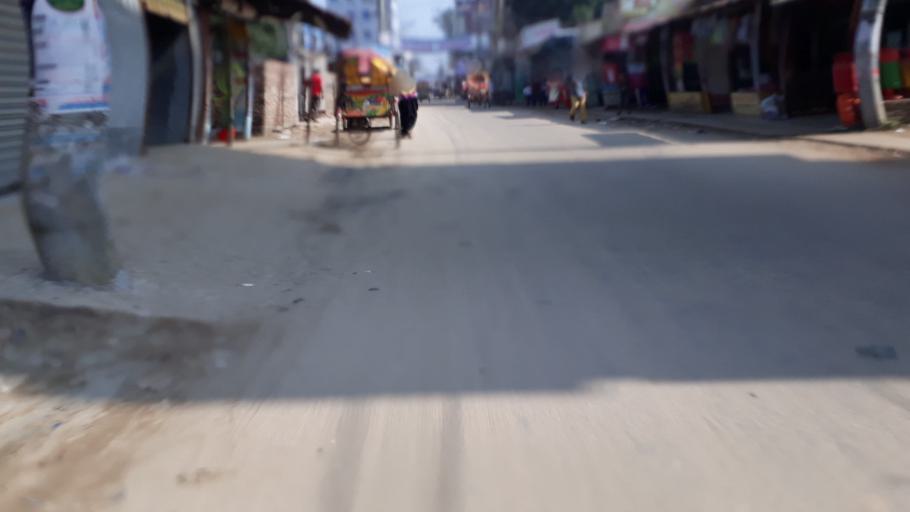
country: BD
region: Dhaka
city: Tungi
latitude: 23.8485
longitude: 90.2738
